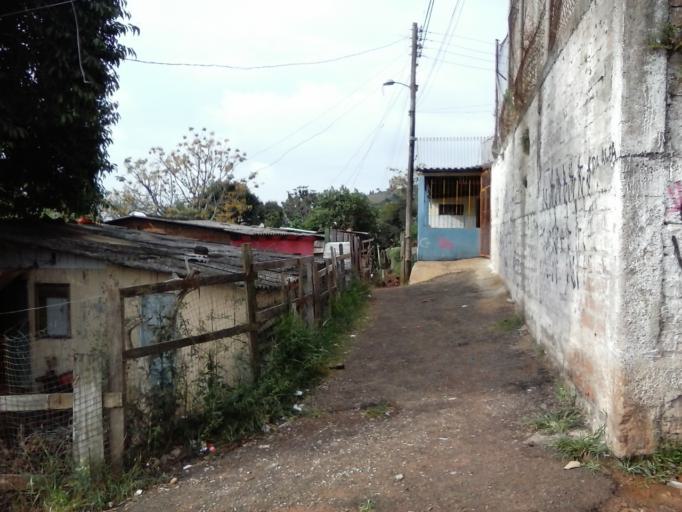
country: BR
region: Rio Grande do Sul
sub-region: Porto Alegre
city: Porto Alegre
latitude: -30.0592
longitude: -51.1428
